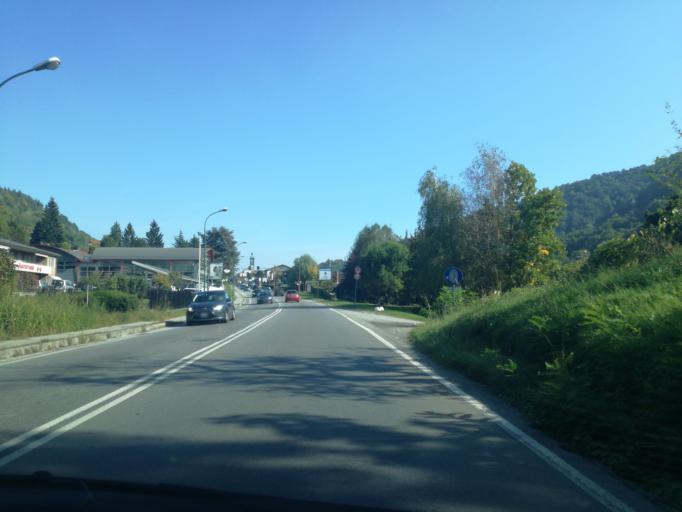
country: IT
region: Lombardy
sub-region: Provincia di Bergamo
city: Caprino
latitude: 45.7326
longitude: 9.4946
